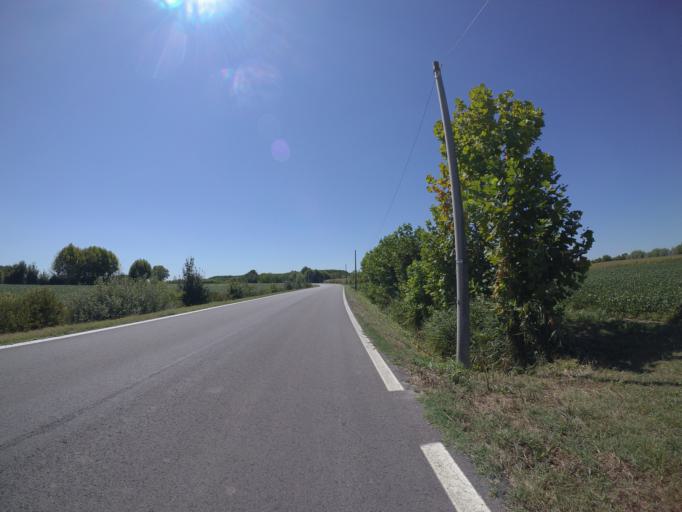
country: IT
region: Friuli Venezia Giulia
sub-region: Provincia di Udine
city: Rivignano
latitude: 45.8606
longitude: 13.0274
